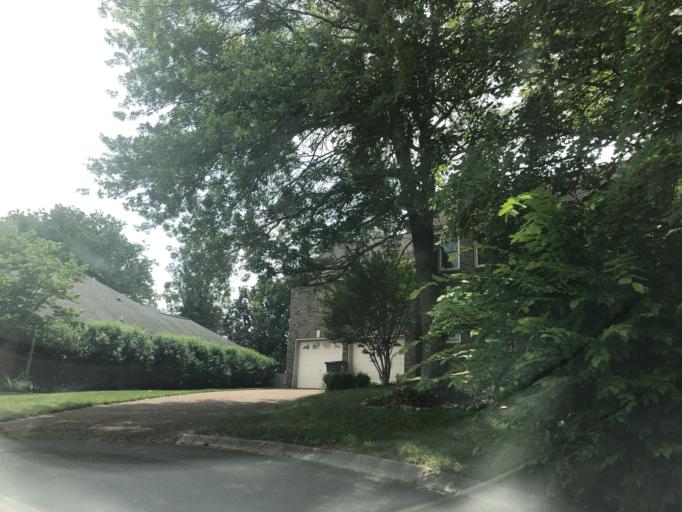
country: US
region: Tennessee
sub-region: Cheatham County
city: Pegram
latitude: 36.0527
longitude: -86.9575
